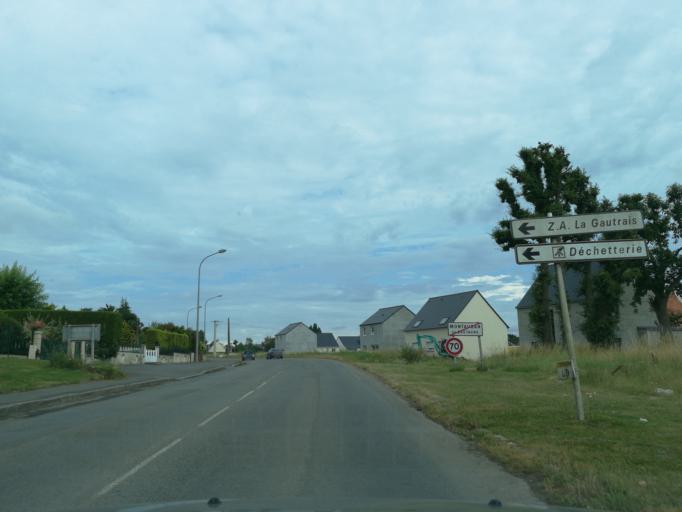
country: FR
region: Brittany
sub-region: Departement d'Ille-et-Vilaine
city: Montauban-de-Bretagne
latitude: 48.1953
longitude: -2.0367
